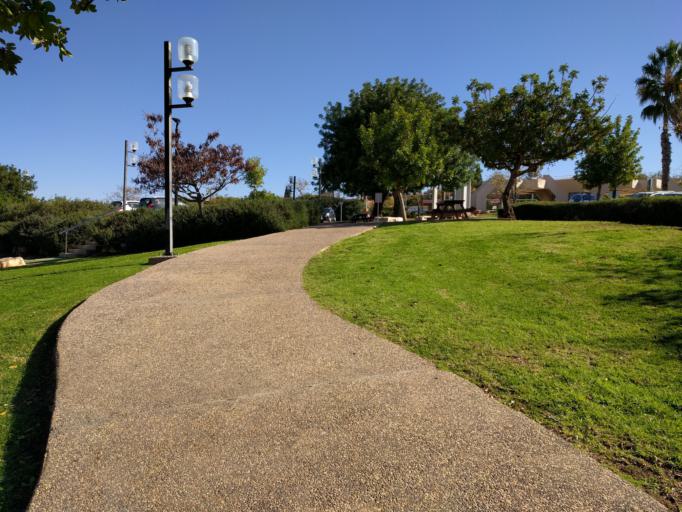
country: IL
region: Northern District
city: Karmi'el
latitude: 32.9133
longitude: 35.2827
